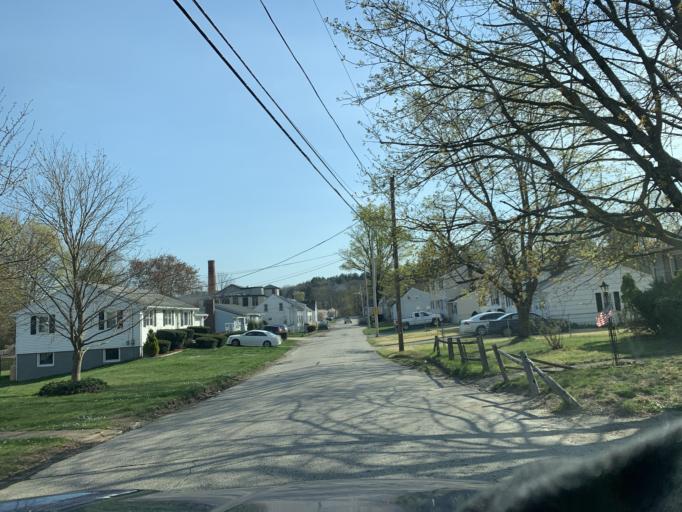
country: US
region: Rhode Island
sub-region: Kent County
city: West Warwick
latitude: 41.7273
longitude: -71.5355
